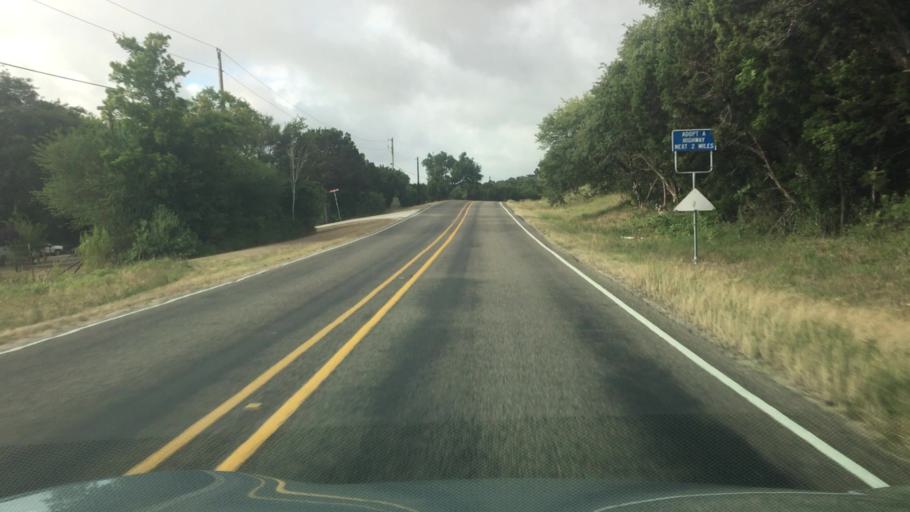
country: US
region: Texas
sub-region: Hays County
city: Dripping Springs
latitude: 30.1632
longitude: -98.2454
